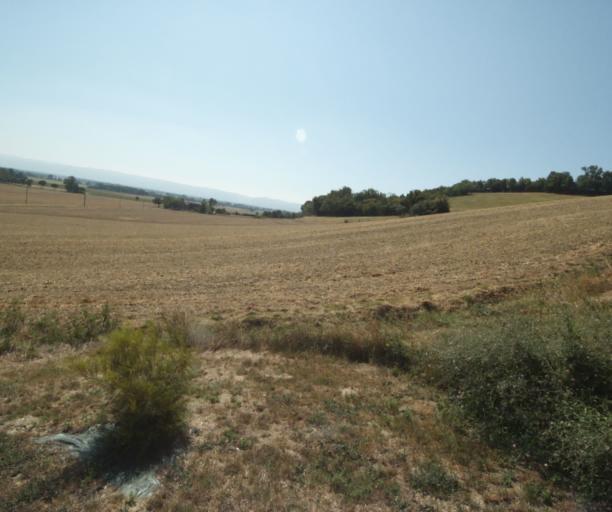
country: FR
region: Midi-Pyrenees
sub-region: Departement du Tarn
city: Puylaurens
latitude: 43.5195
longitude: 1.9423
